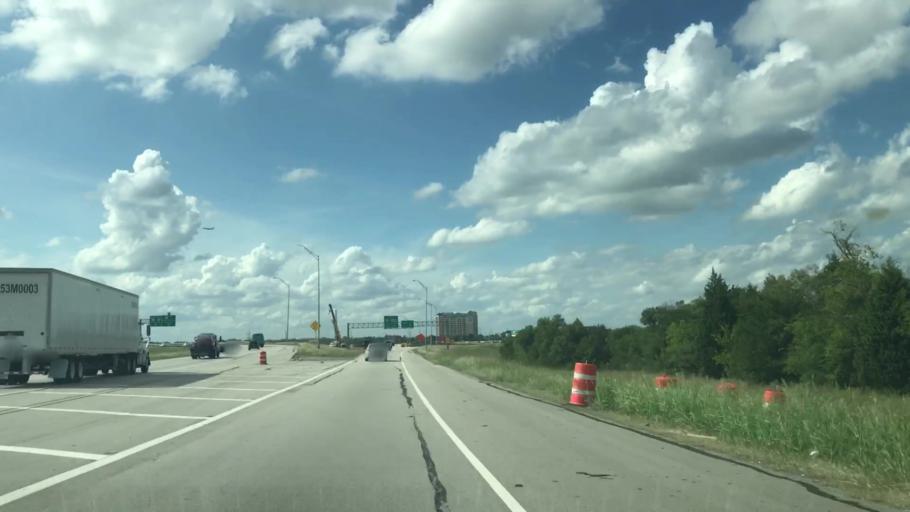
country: US
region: Texas
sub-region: Dallas County
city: Coppell
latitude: 32.9499
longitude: -97.0341
